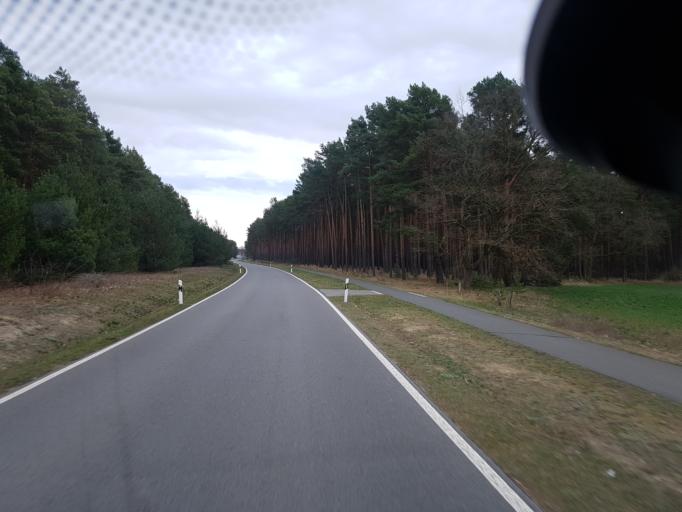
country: DE
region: Brandenburg
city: Mixdorf
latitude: 52.1982
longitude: 14.3826
